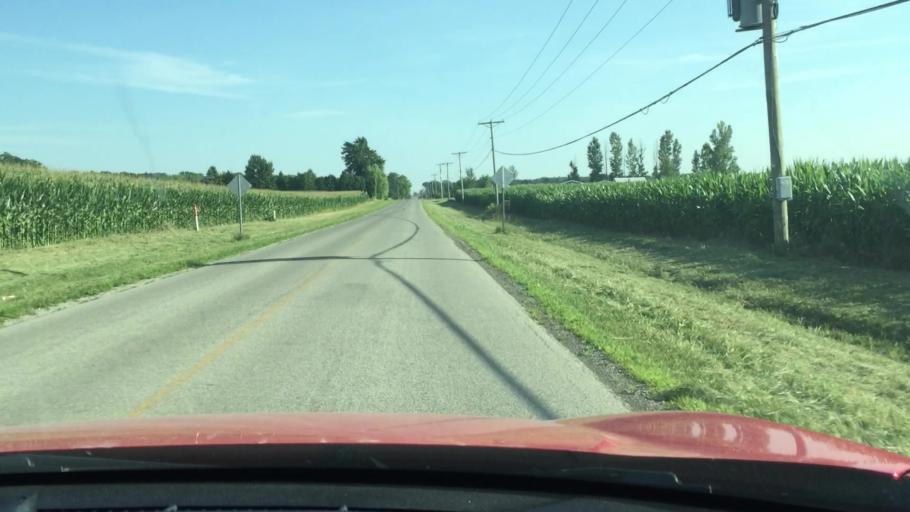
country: US
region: Ohio
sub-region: Hardin County
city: Ada
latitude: 40.7459
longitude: -83.8424
